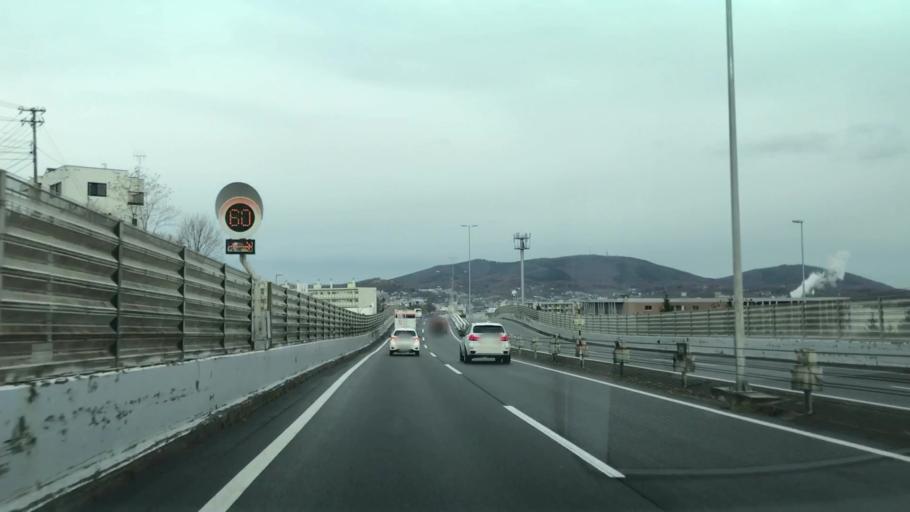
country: JP
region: Hokkaido
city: Otaru
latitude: 43.1803
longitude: 141.0211
